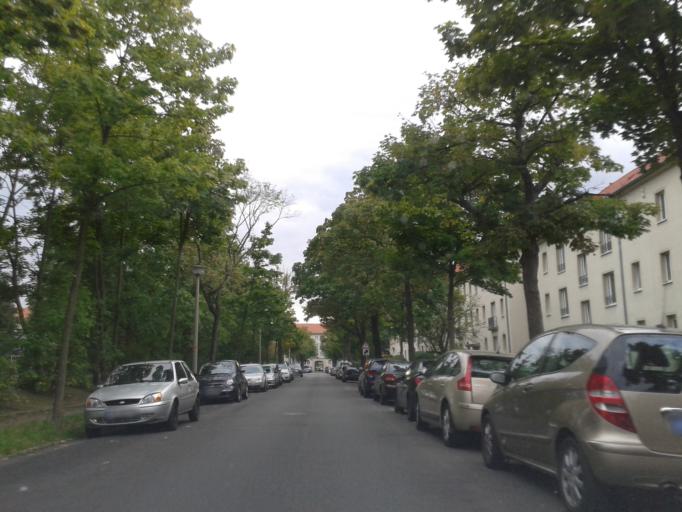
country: DE
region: Saxony
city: Dresden
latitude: 51.0385
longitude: 13.7232
